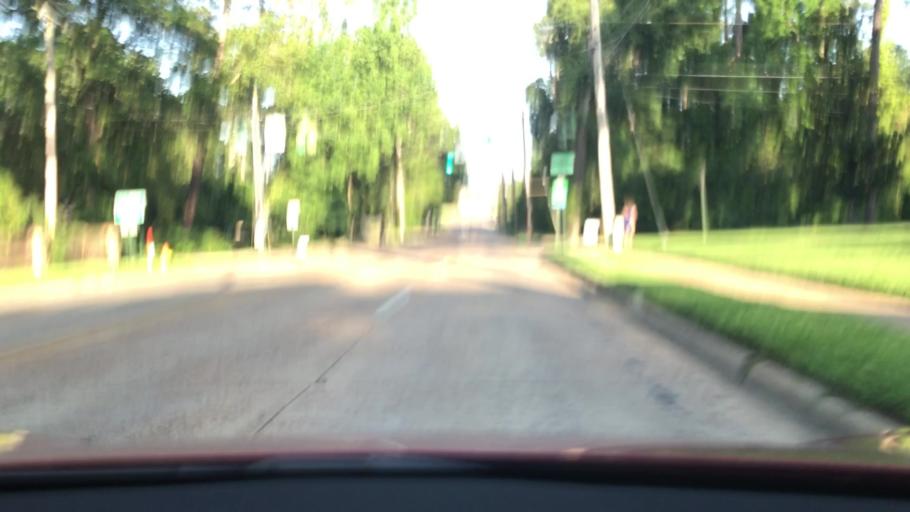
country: US
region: Louisiana
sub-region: Bossier Parish
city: Bossier City
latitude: 32.4548
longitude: -93.7413
